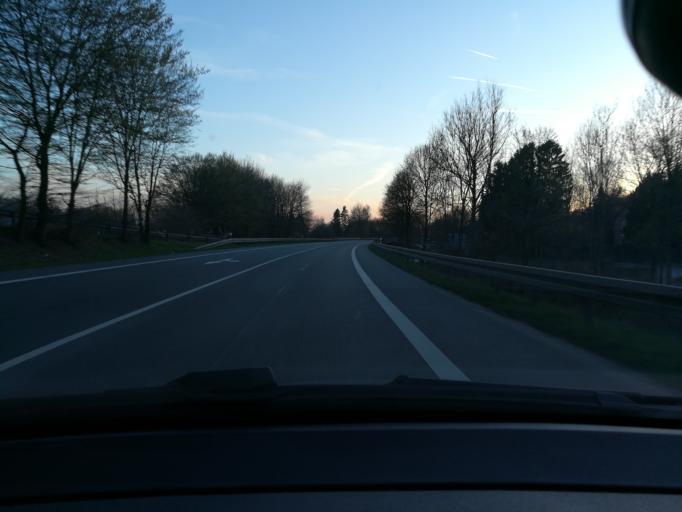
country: DE
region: North Rhine-Westphalia
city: Halle
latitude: 52.0715
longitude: 8.3642
